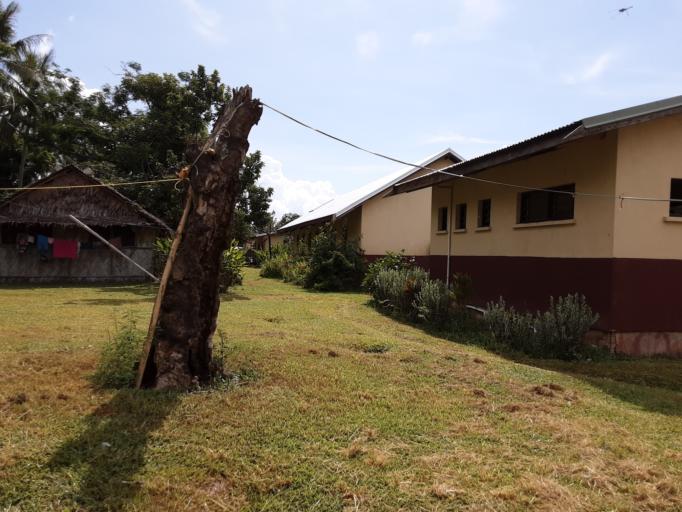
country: VU
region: Sanma
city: Luganville
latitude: -15.5801
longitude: 166.9996
